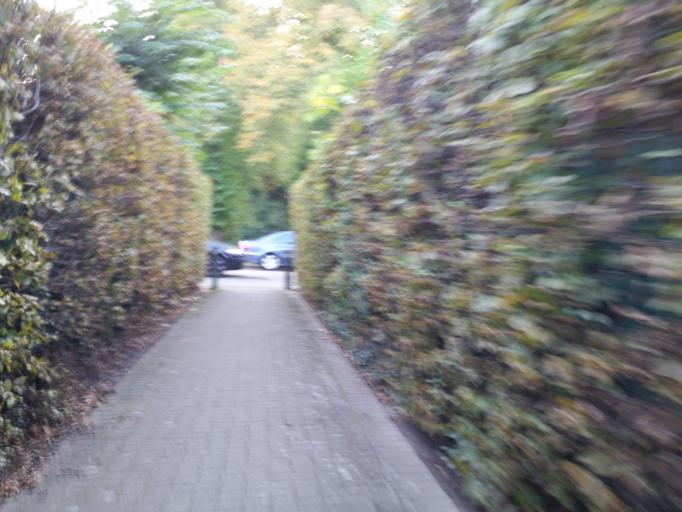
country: BE
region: Flanders
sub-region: Provincie Antwerpen
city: Niel
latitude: 51.0980
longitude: 4.3411
